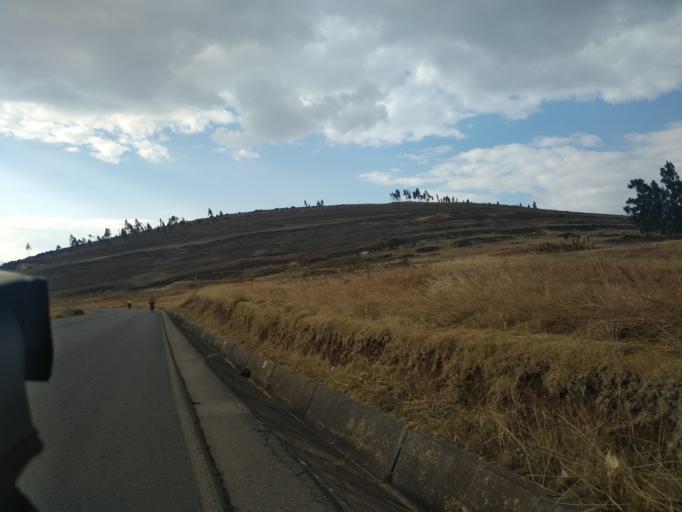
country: PE
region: Cajamarca
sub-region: Provincia de Cajamarca
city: Llacanora
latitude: -7.1463
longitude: -78.3991
